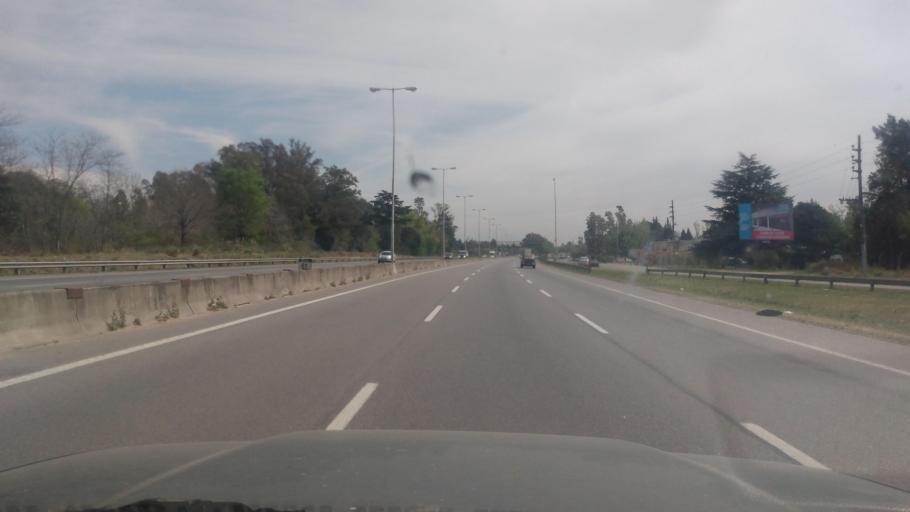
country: AR
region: Buenos Aires
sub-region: Partido de Pilar
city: Pilar
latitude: -34.4380
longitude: -58.9807
